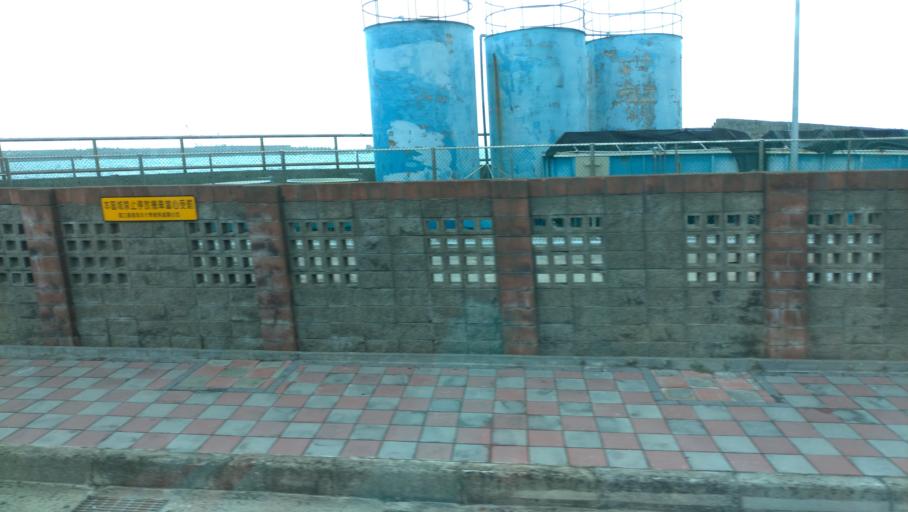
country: TW
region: Taiwan
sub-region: Keelung
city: Keelung
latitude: 25.1509
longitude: 121.7788
